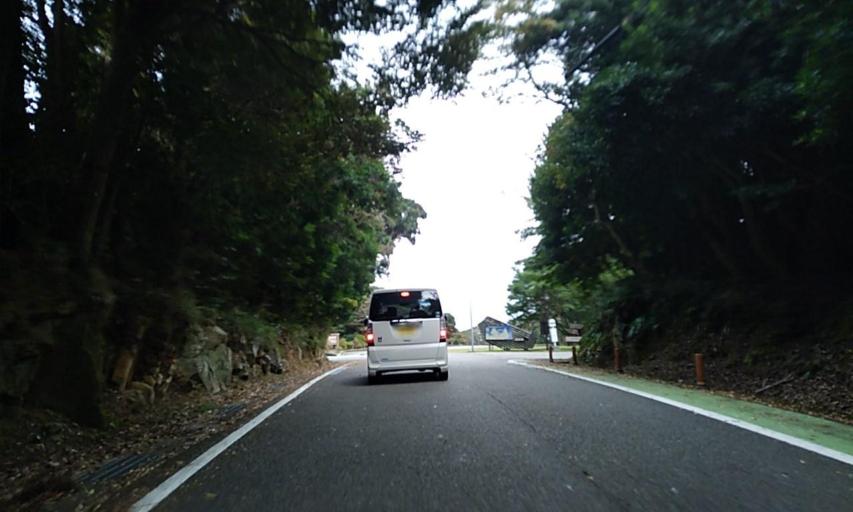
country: JP
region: Wakayama
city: Shingu
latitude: 33.5828
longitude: 135.9557
